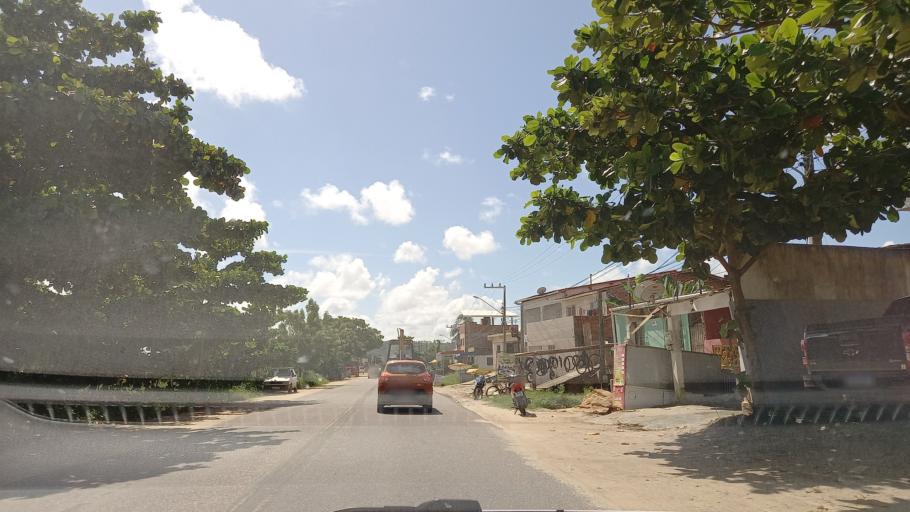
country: BR
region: Pernambuco
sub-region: Sao Jose Da Coroa Grande
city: Sao Jose da Coroa Grande
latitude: -8.8907
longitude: -35.1508
